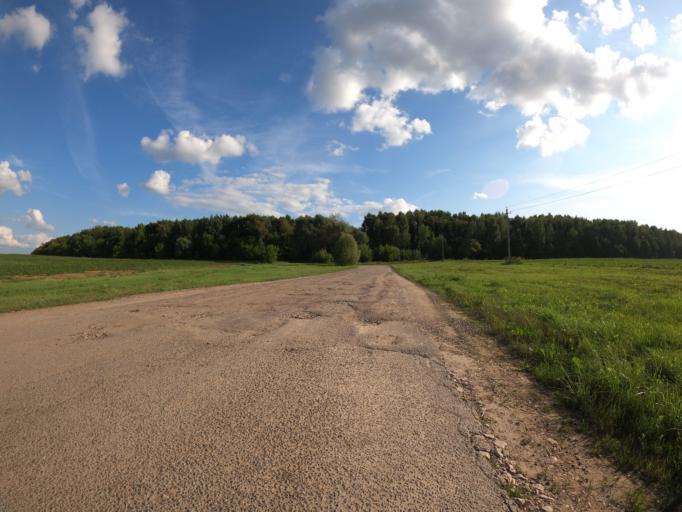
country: RU
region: Moskovskaya
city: Meshcherino
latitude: 55.1827
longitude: 38.4712
